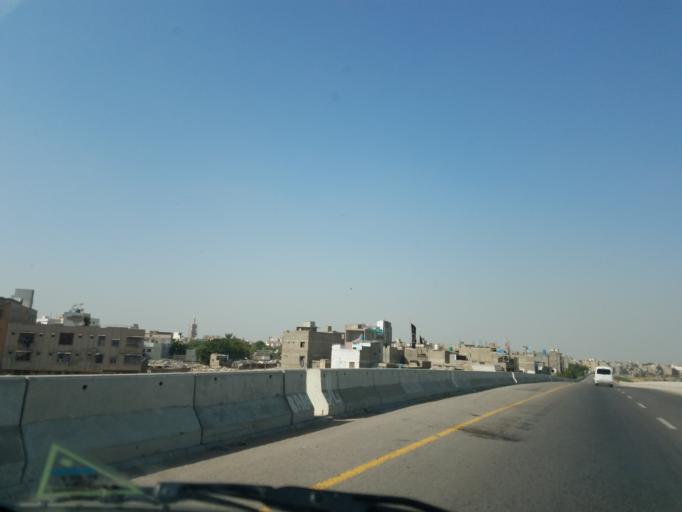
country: PK
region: Sindh
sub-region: Karachi District
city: Karachi
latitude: 24.9171
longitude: 67.0784
